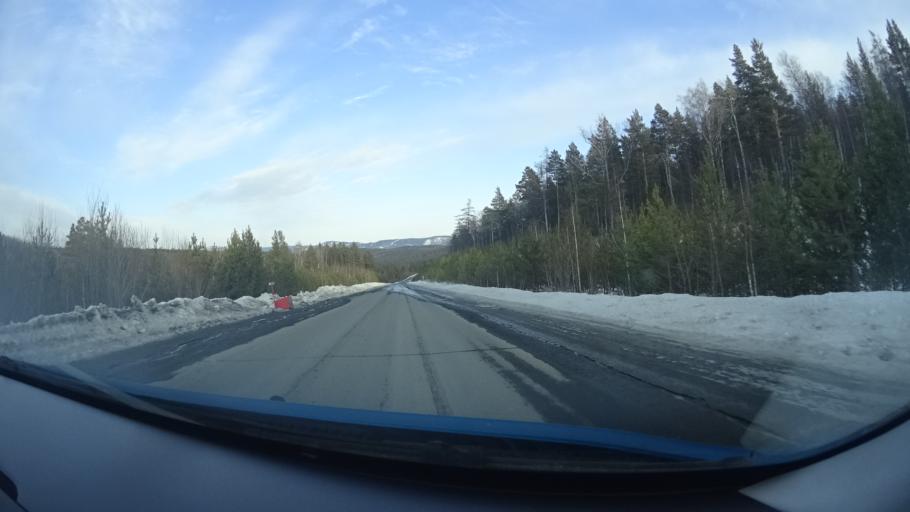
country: RU
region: Bashkortostan
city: Lomovka
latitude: 53.5237
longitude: 58.2761
